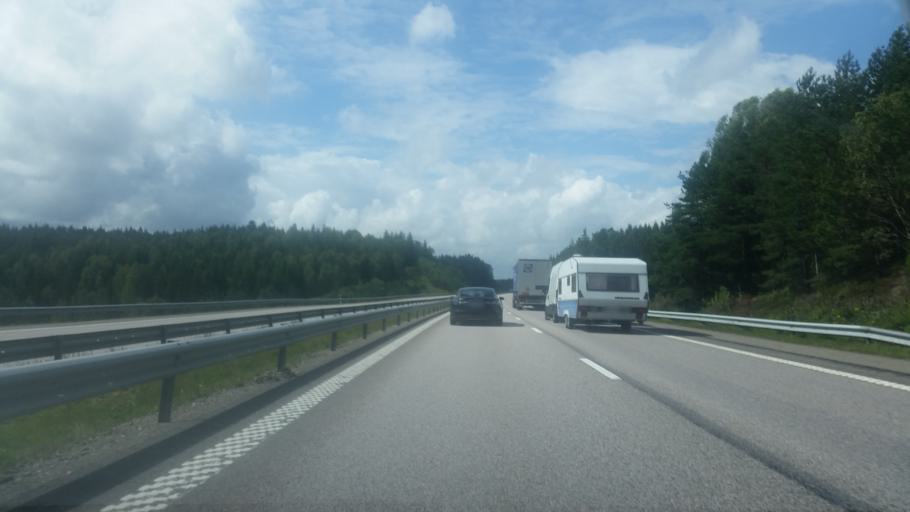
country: SE
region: Vaestra Goetaland
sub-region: Bollebygds Kommun
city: Bollebygd
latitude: 57.6702
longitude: 12.6441
